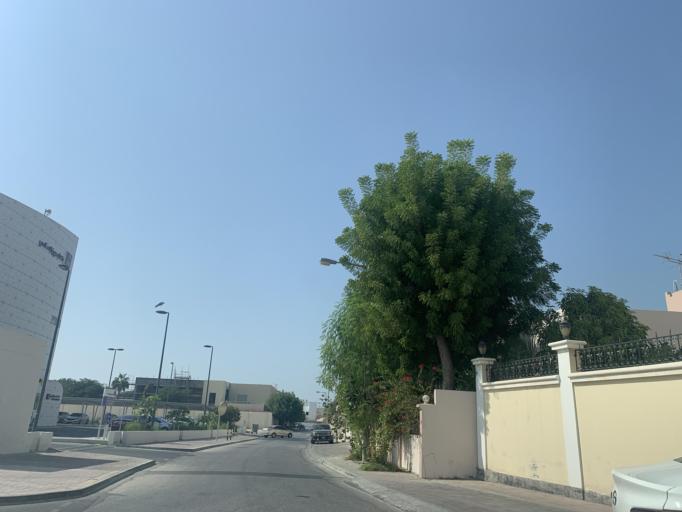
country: BH
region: Central Governorate
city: Madinat Hamad
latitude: 26.1348
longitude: 50.4958
